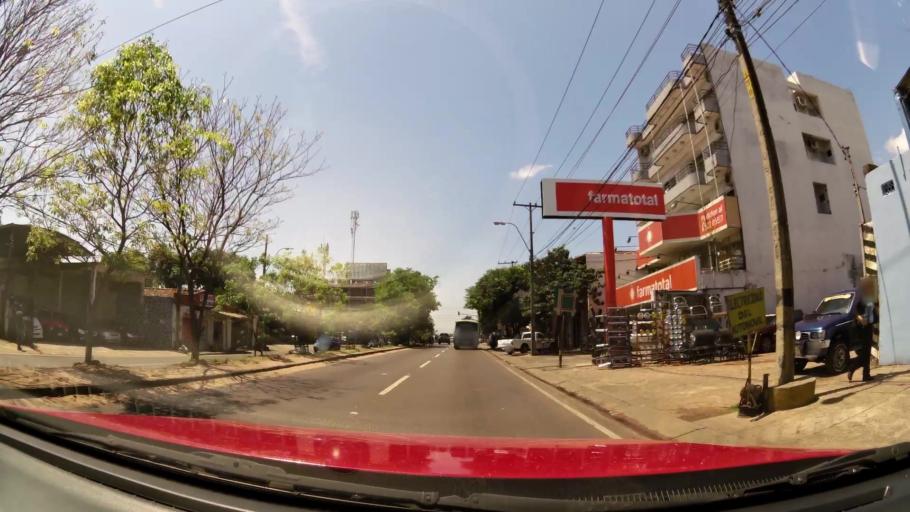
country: PY
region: Central
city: Lambare
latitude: -25.3314
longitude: -57.5748
